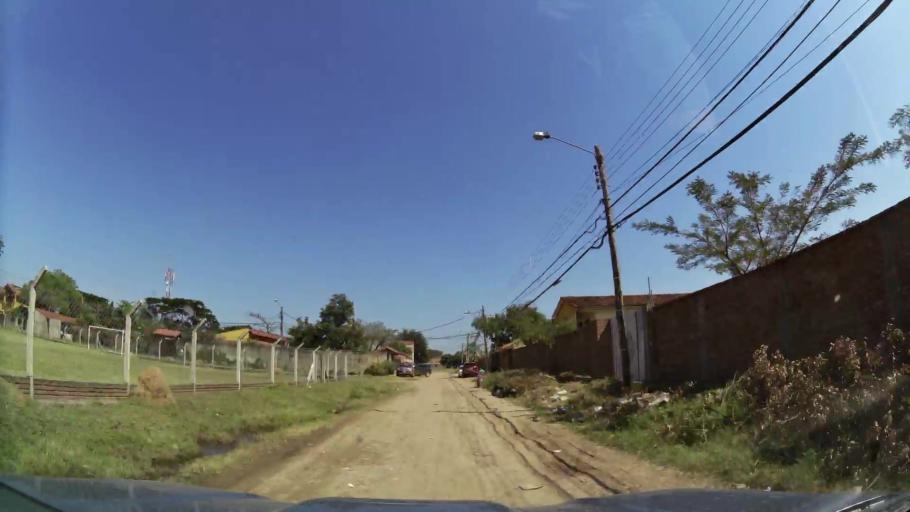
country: BO
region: Santa Cruz
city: Santa Cruz de la Sierra
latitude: -17.7367
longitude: -63.1526
